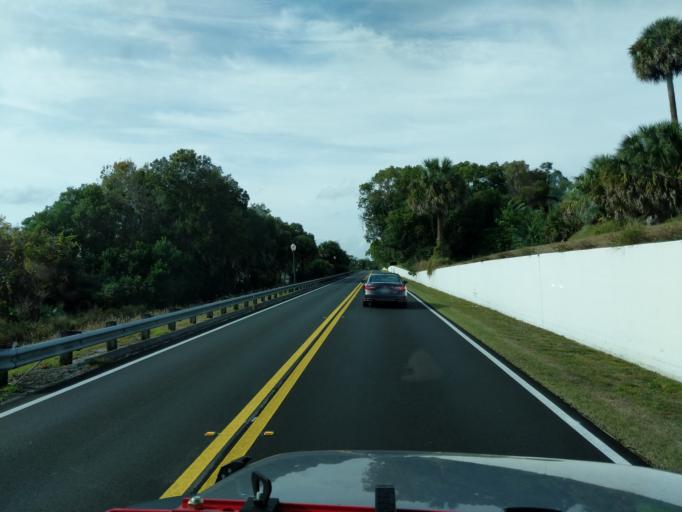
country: US
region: Florida
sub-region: Lake County
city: Mount Dora
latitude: 28.8039
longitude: -81.6512
